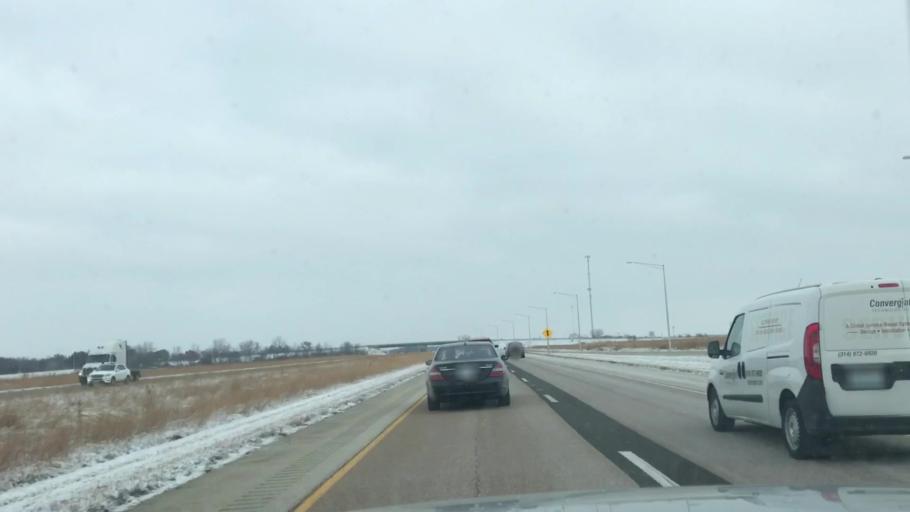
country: US
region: Illinois
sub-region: Montgomery County
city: Litchfield
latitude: 39.2288
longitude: -89.6436
